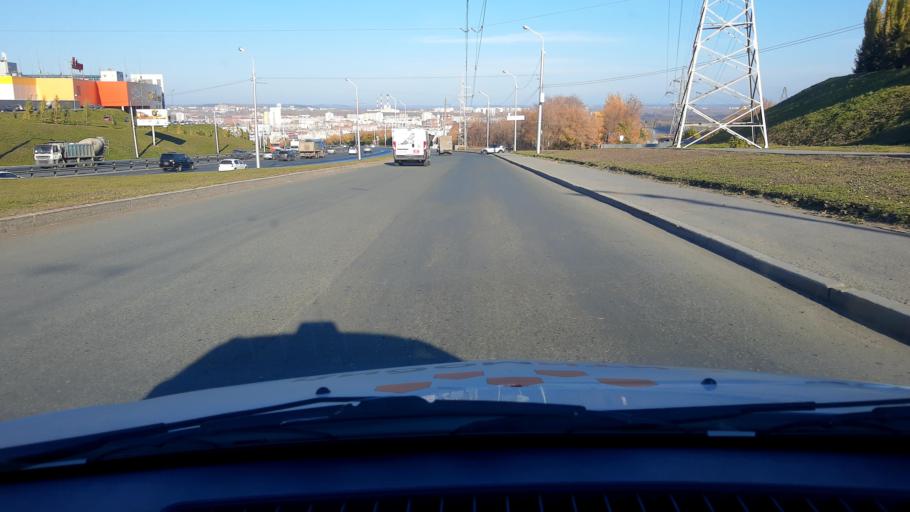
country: RU
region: Bashkortostan
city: Ufa
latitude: 54.7542
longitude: 56.0333
